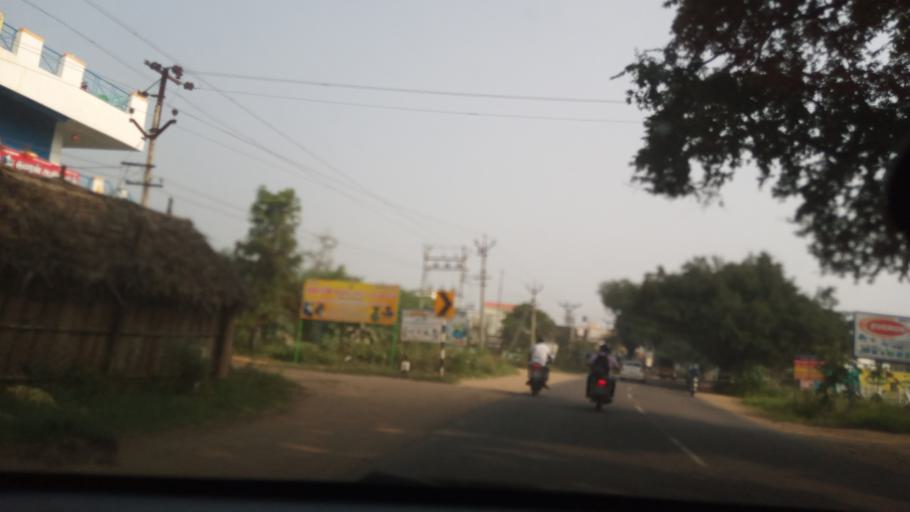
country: IN
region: Tamil Nadu
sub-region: Coimbatore
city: Annur
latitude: 11.1680
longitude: 77.0532
